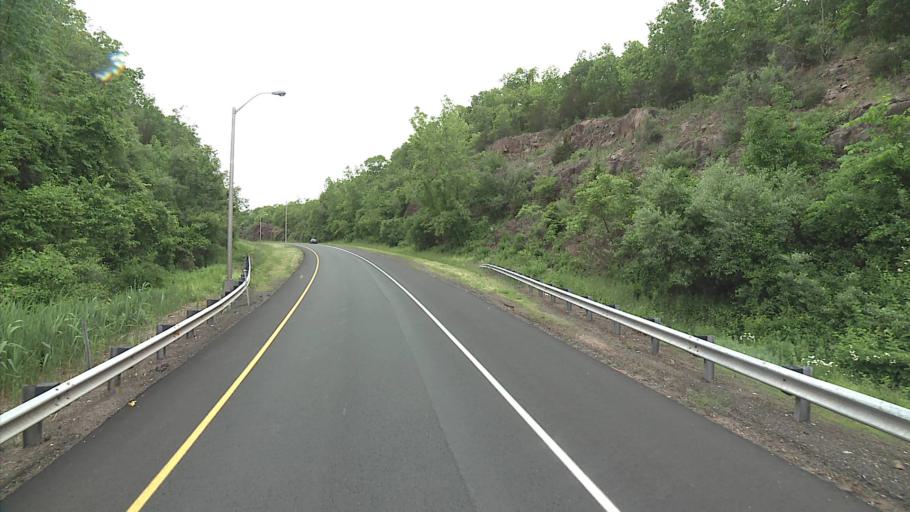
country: US
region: Connecticut
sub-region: Middlesex County
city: Cromwell
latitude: 41.6246
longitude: -72.6942
